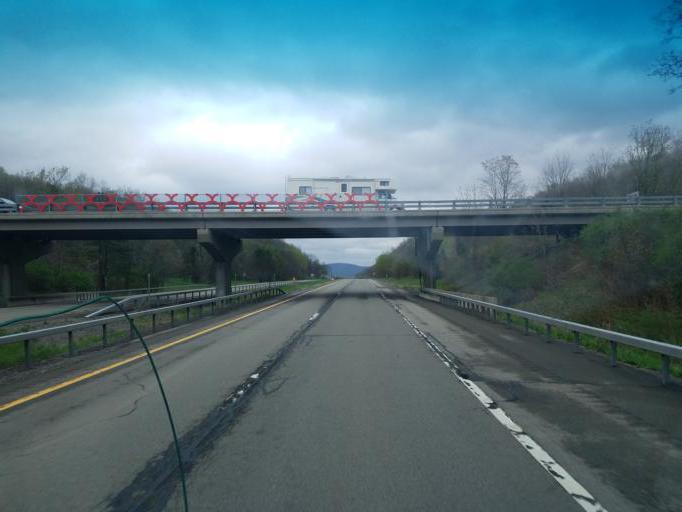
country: US
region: New York
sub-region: Cattaraugus County
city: Randolph
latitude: 42.0992
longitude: -78.8484
